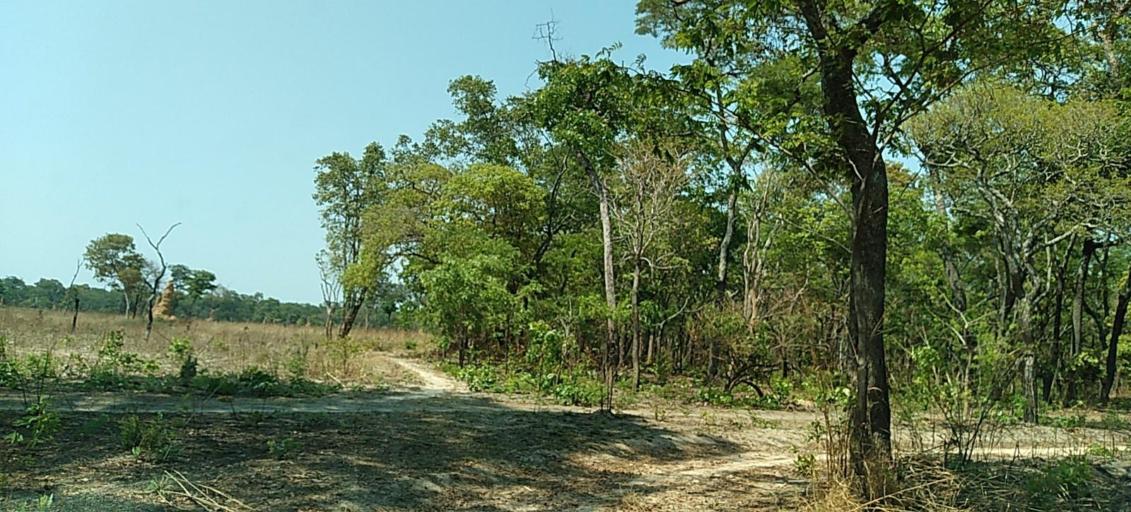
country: ZM
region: Copperbelt
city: Mpongwe
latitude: -13.7893
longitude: 28.0981
